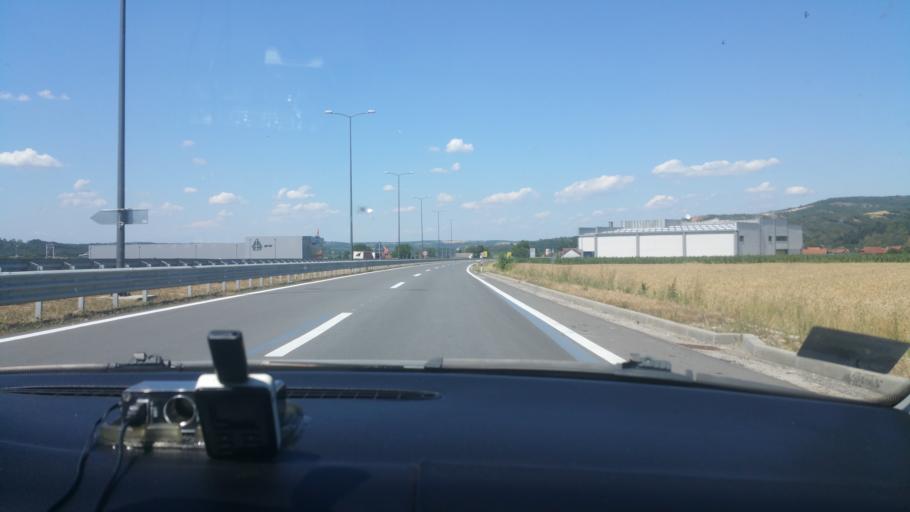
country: RS
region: Central Serbia
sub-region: Sumadijski Okrug
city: Batocina
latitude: 44.1173
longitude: 21.0106
